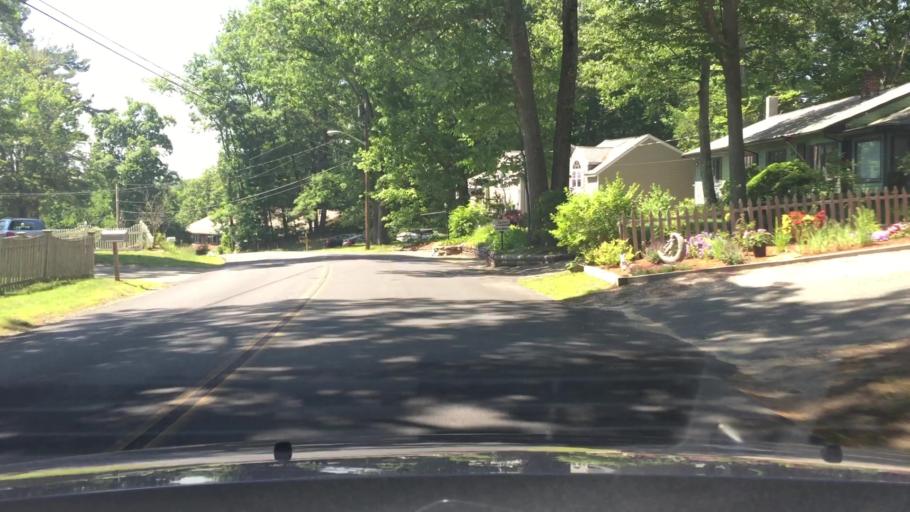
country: US
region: New Hampshire
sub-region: Rockingham County
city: Plaistow
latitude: 42.8202
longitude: -71.0986
